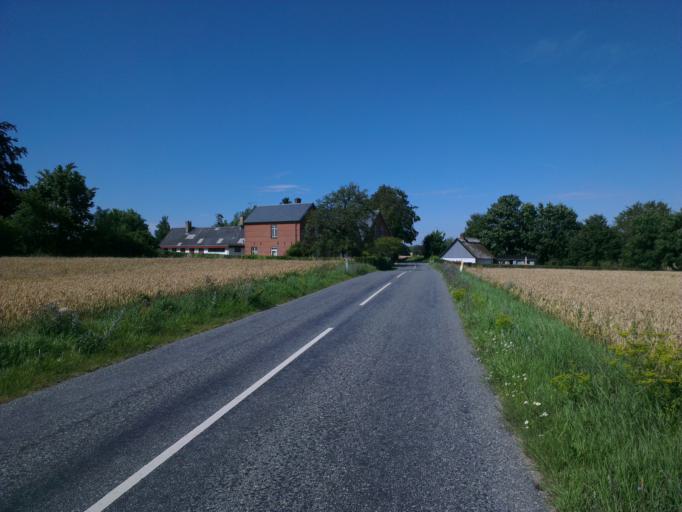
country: DK
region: Capital Region
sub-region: Frederikssund Kommune
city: Frederikssund
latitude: 55.8695
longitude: 12.0884
